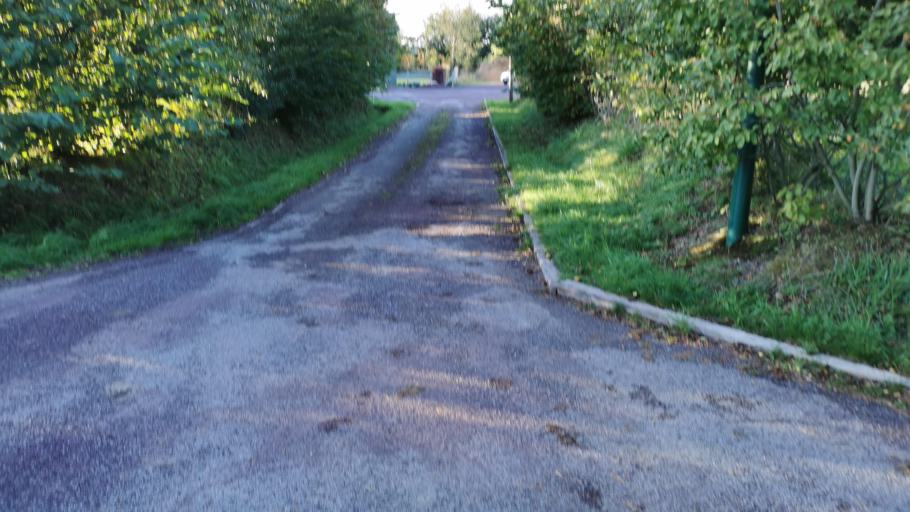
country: FR
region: Brittany
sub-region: Departement du Morbihan
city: Mauron
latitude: 48.0902
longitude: -2.2603
